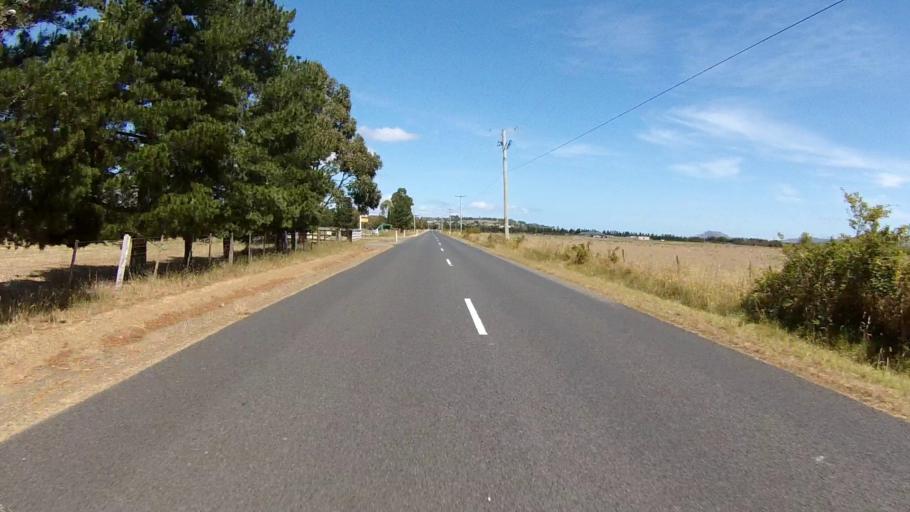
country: AU
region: Tasmania
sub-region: Sorell
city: Sorell
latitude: -42.7721
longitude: 147.5180
